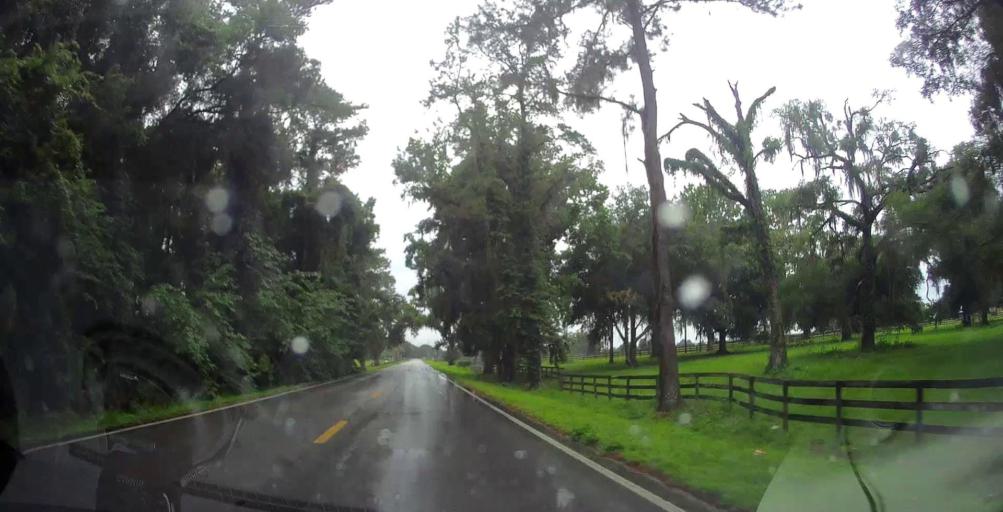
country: US
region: Florida
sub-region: Marion County
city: Citra
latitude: 29.3368
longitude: -82.2096
